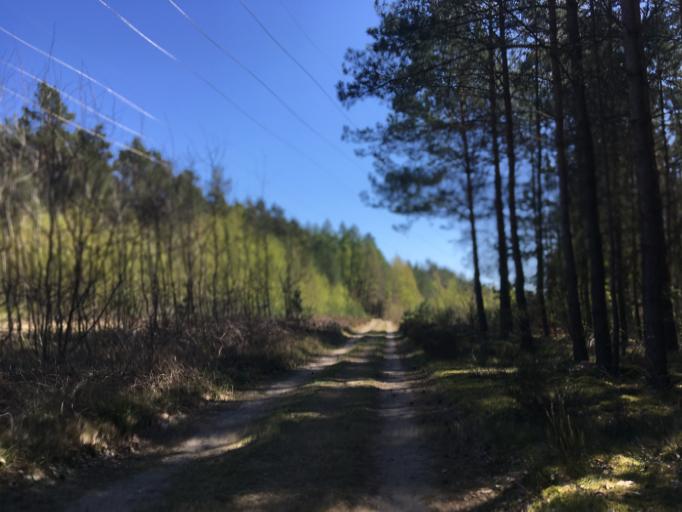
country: DE
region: Brandenburg
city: Bernau bei Berlin
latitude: 52.7024
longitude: 13.5293
